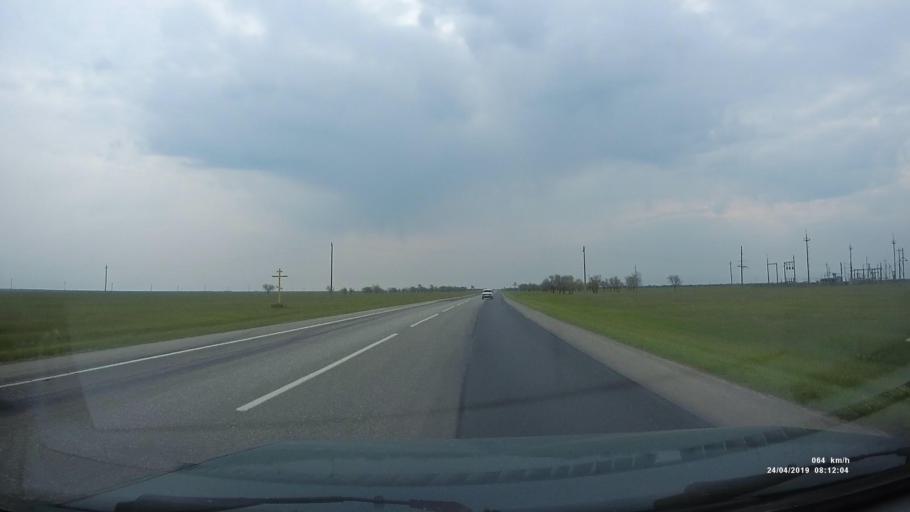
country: RU
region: Kalmykiya
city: Priyutnoye
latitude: 46.1033
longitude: 43.5359
